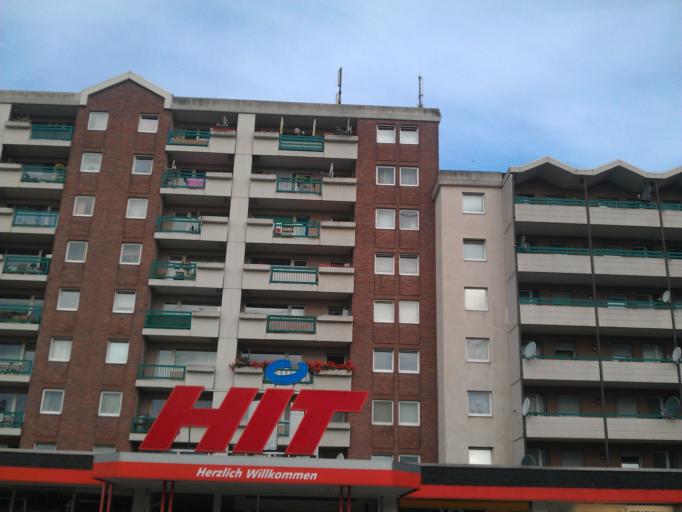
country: NL
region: Limburg
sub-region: Gemeente Vaals
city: Vaals
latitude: 50.7709
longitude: 6.0402
